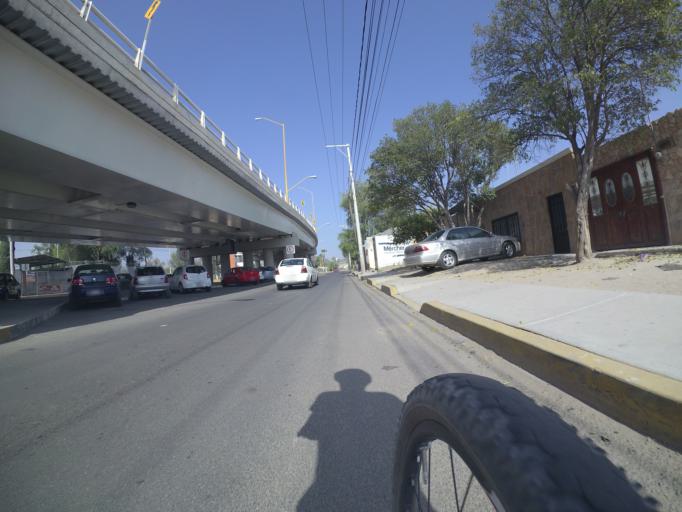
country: MX
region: Aguascalientes
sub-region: Jesus Maria
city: Corral de Barrancos
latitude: 21.9527
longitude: -102.3339
